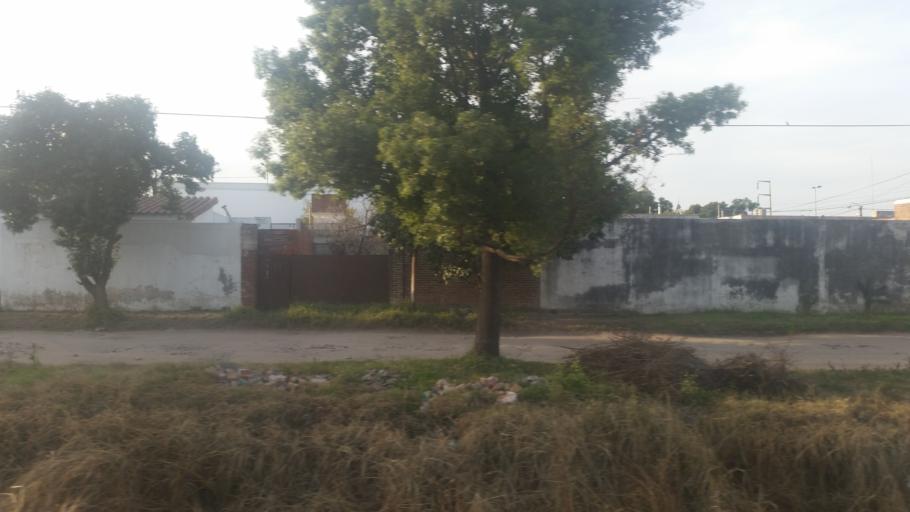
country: AR
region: Cordoba
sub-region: Departamento de Capital
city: Cordoba
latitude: -31.4332
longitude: -64.1371
